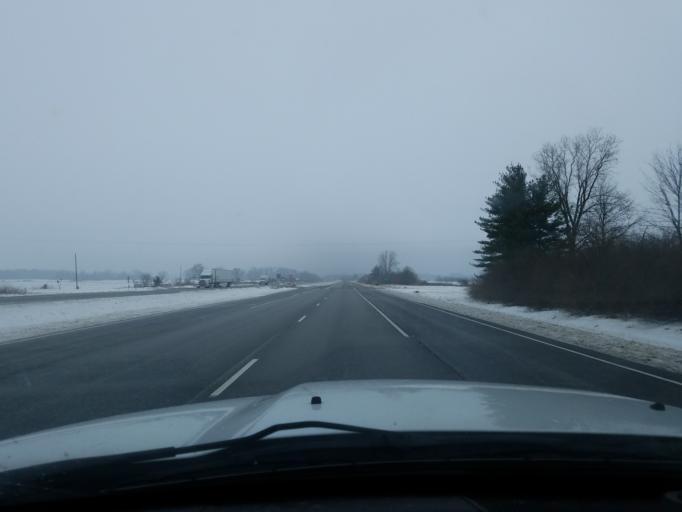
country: US
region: Indiana
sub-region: Fulton County
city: Rochester
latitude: 40.9950
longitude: -86.1677
